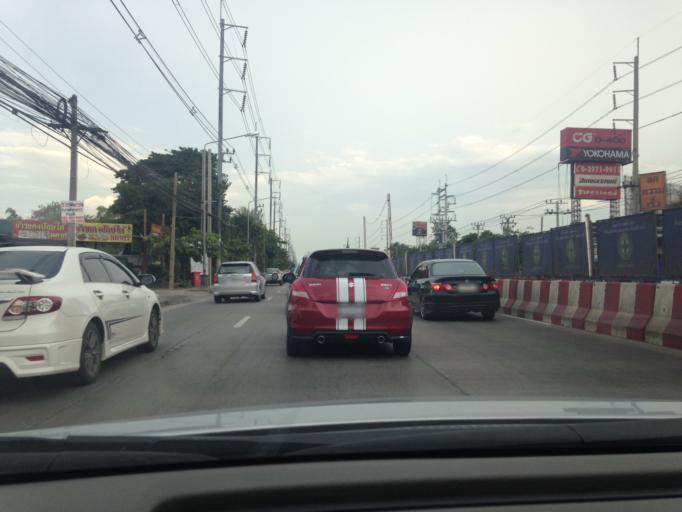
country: TH
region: Bangkok
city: Bang Khen
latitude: 13.8622
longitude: 100.6192
